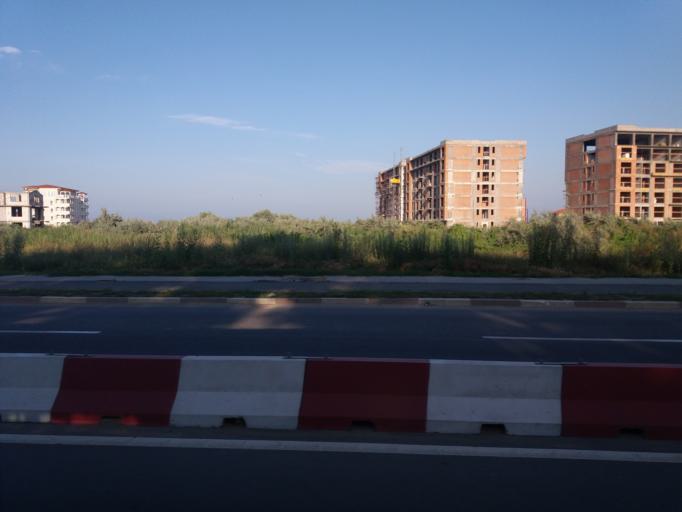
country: RO
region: Constanta
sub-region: Comuna Navodari
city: Navodari
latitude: 44.2906
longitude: 28.6189
